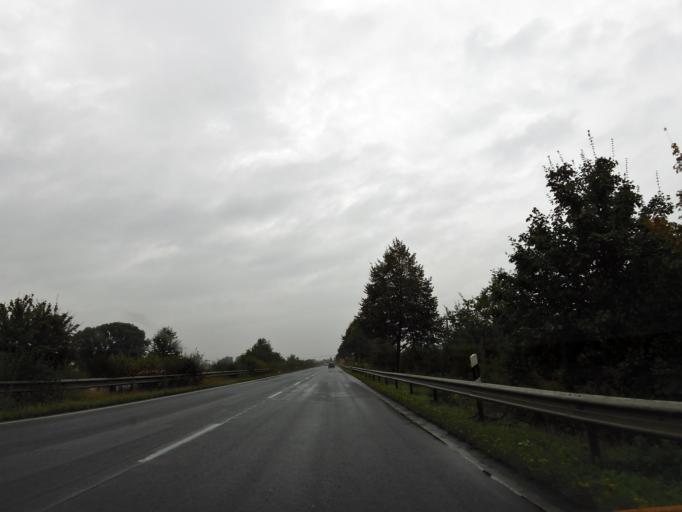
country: DE
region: Lower Saxony
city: Bovenden
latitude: 51.5740
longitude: 9.9217
